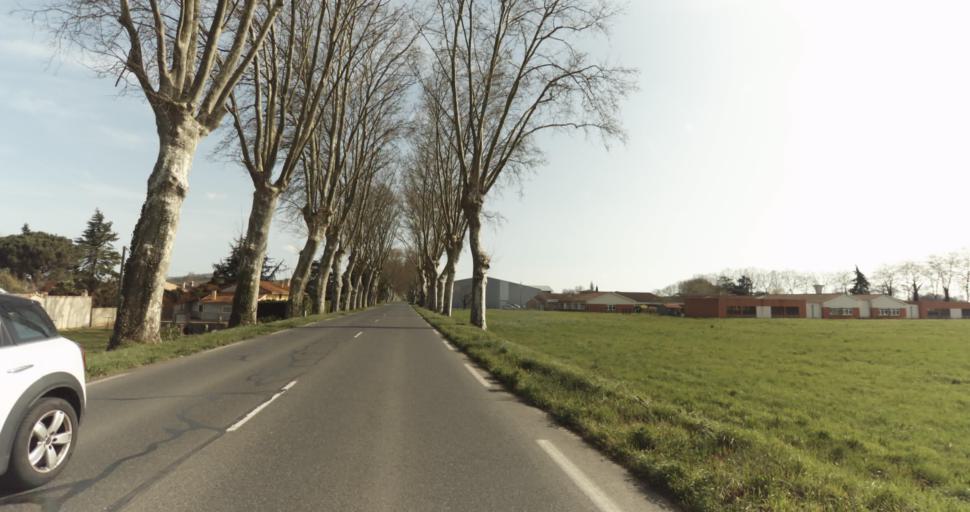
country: FR
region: Midi-Pyrenees
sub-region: Departement du Tarn
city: Saint-Sulpice-la-Pointe
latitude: 43.7769
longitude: 1.6670
